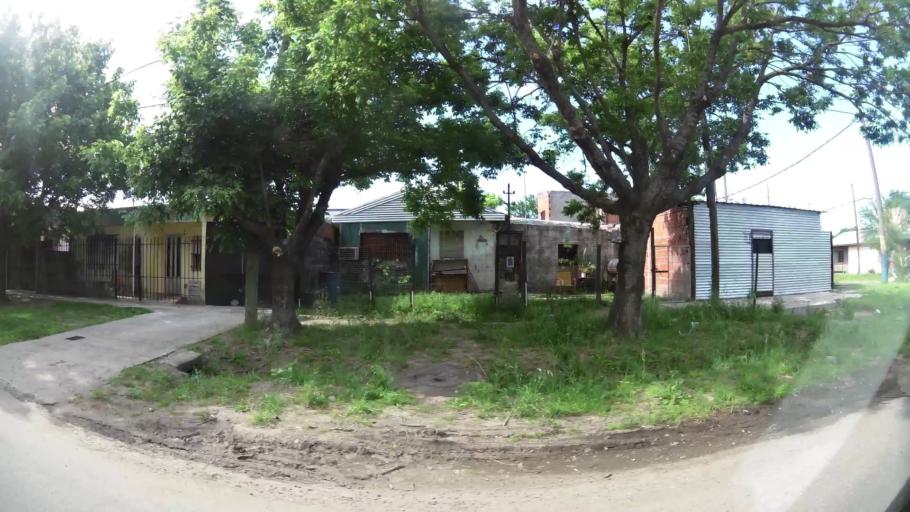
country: AR
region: Santa Fe
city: Granadero Baigorria
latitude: -32.9244
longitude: -60.7159
